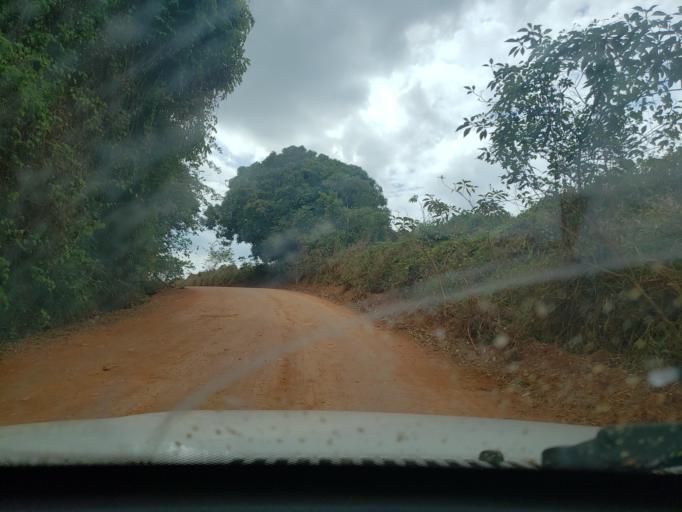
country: BR
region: Minas Gerais
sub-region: Boa Esperanca
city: Boa Esperanca
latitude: -20.9811
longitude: -45.5950
